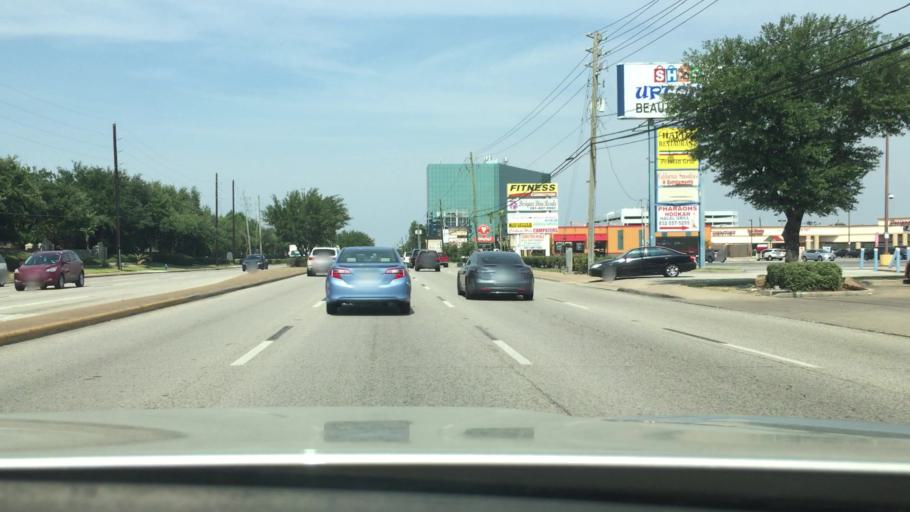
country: US
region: Texas
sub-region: Harris County
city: Bunker Hill Village
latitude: 29.7368
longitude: -95.5765
